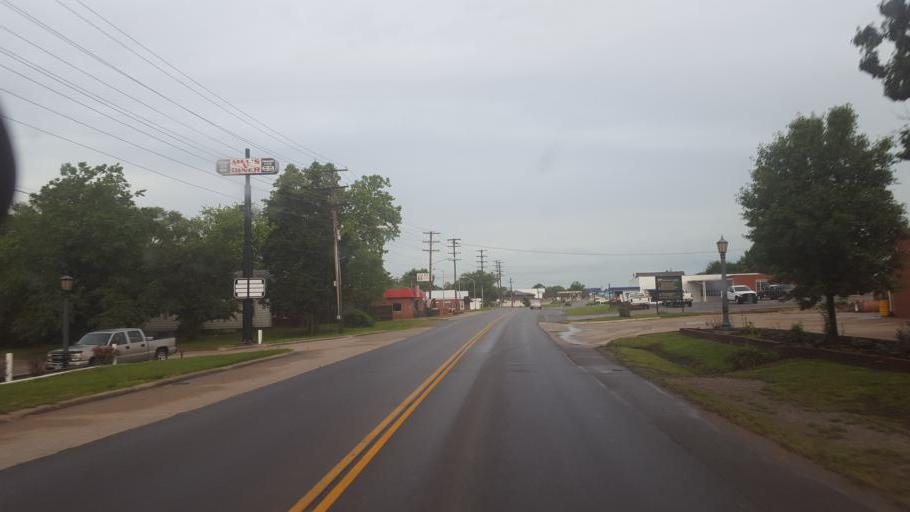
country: US
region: Missouri
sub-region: Moniteau County
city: California
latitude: 38.6277
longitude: -92.5713
